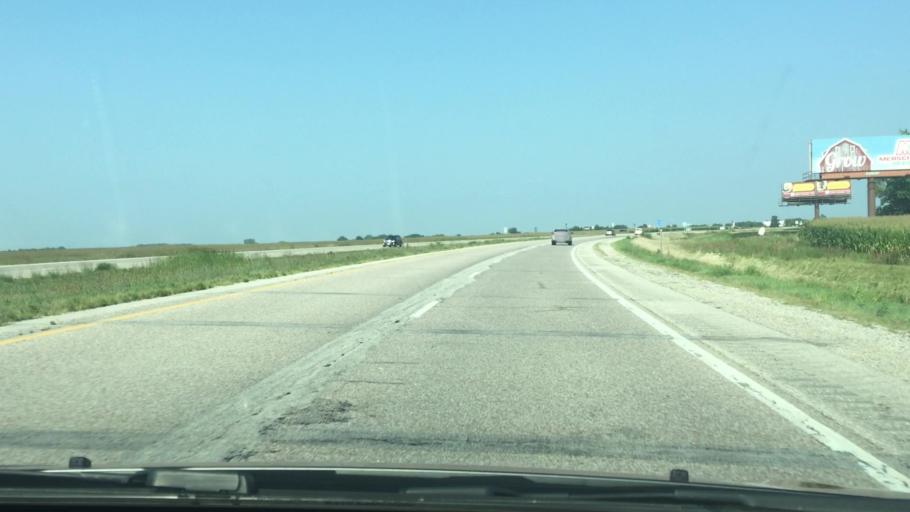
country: US
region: Iowa
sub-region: Muscatine County
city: Muscatine
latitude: 41.4971
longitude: -90.9719
